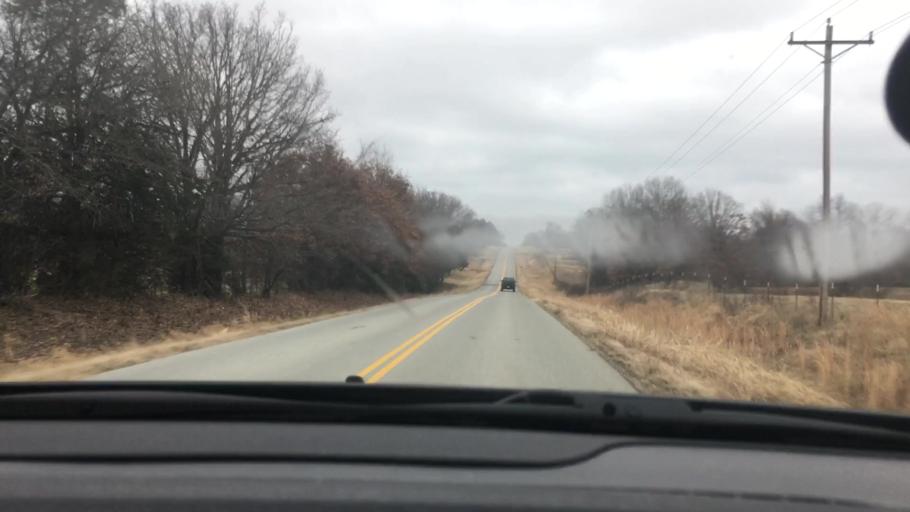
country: US
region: Oklahoma
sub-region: Atoka County
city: Atoka
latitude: 34.3242
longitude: -96.0755
